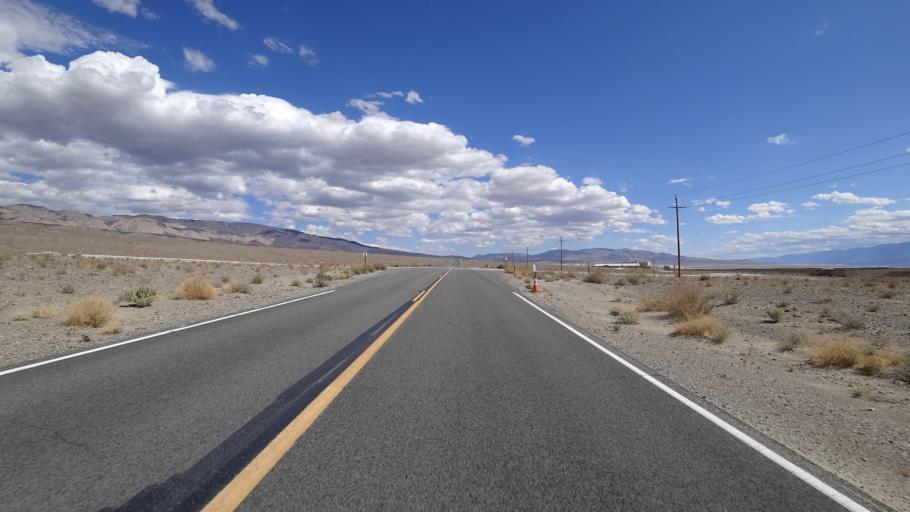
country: US
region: California
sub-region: Inyo County
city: Lone Pine
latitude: 36.4744
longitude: -117.8557
